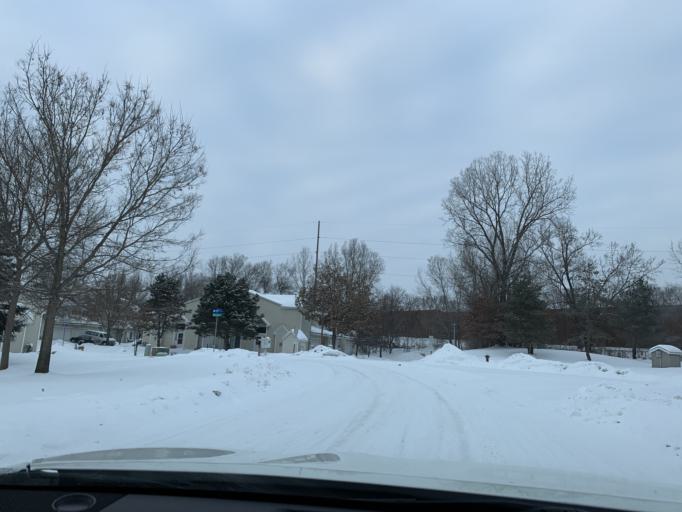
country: US
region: Minnesota
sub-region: Anoka County
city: Coon Rapids
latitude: 45.1668
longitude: -93.2919
